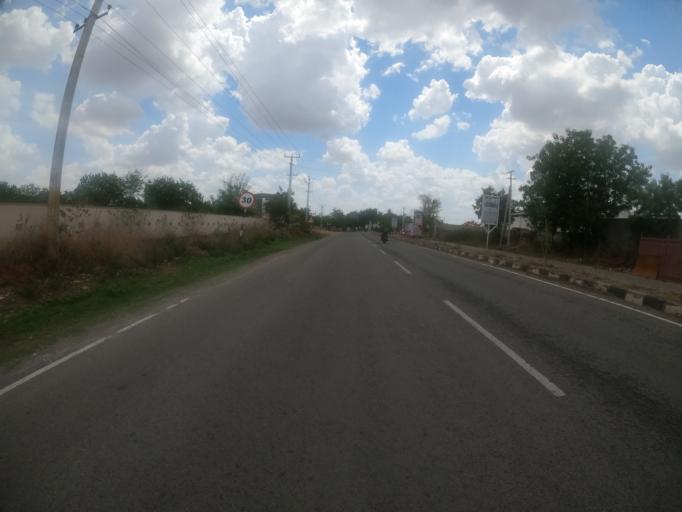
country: IN
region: Telangana
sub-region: Rangareddi
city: Sriramnagar
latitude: 17.3312
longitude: 78.2900
